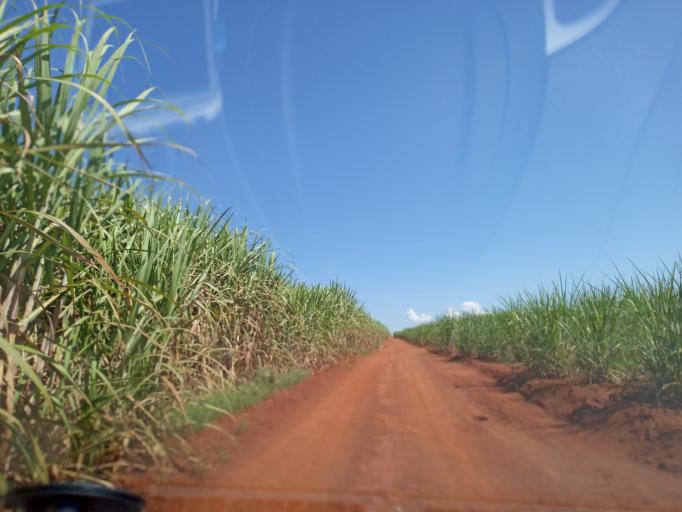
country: BR
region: Goias
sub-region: Itumbiara
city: Itumbiara
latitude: -18.4355
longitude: -49.1504
